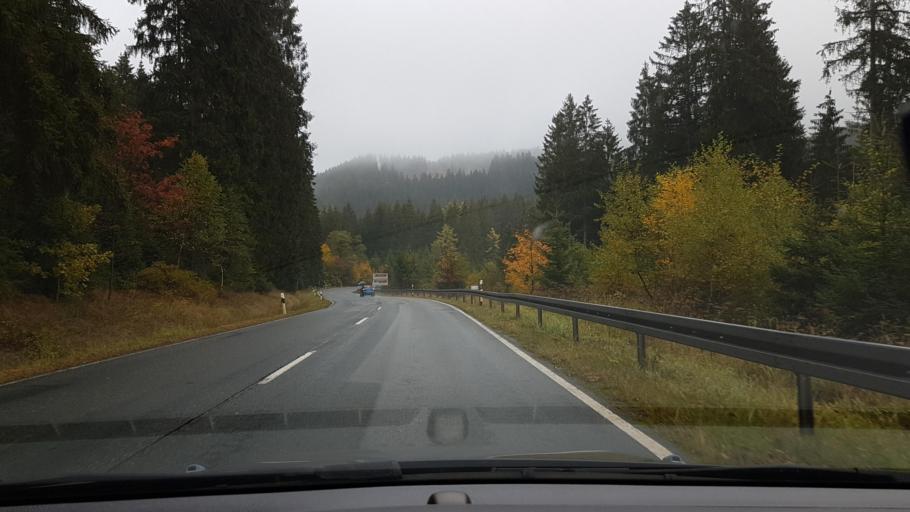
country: DE
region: Lower Saxony
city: Wildemann
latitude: 51.8116
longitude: 10.2768
